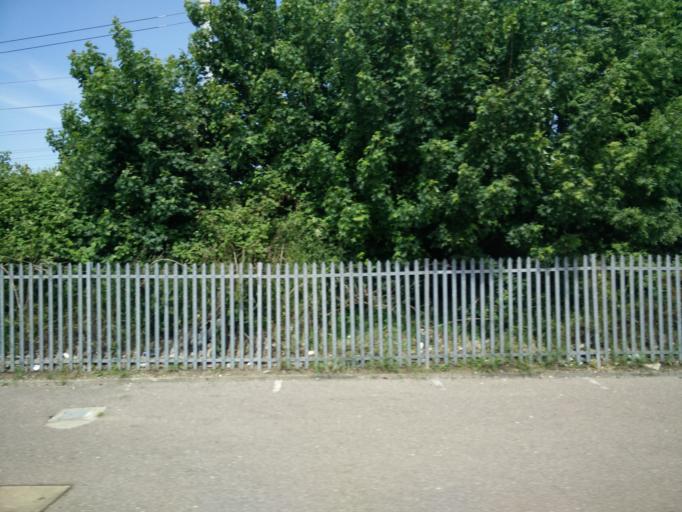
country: GB
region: England
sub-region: Luton
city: Luton
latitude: 51.8816
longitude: -0.4114
